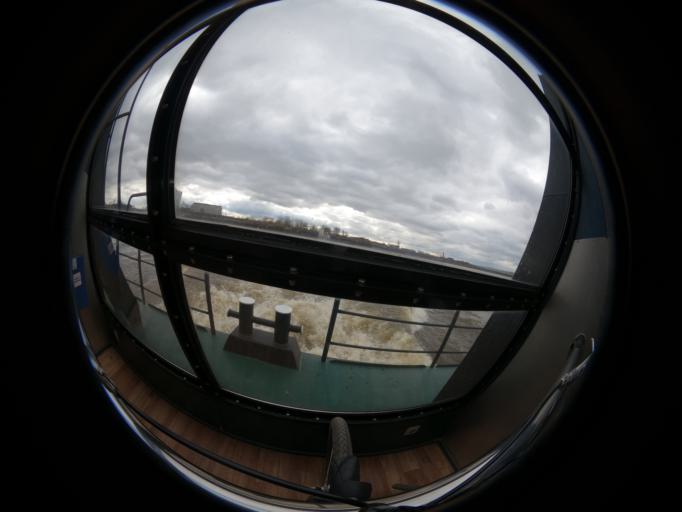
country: DE
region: Hamburg
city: Altona
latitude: 53.5449
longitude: 9.8614
